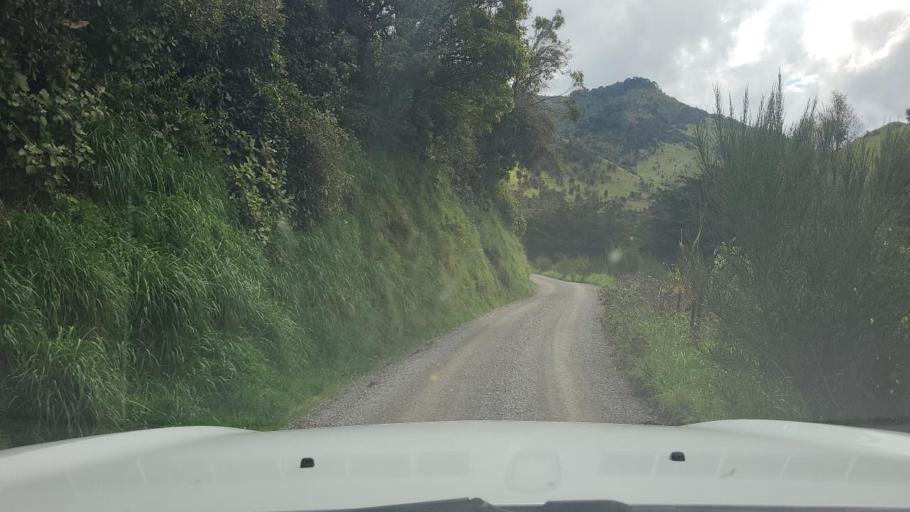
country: NZ
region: Wellington
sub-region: Masterton District
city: Masterton
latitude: -40.9310
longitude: 175.4941
